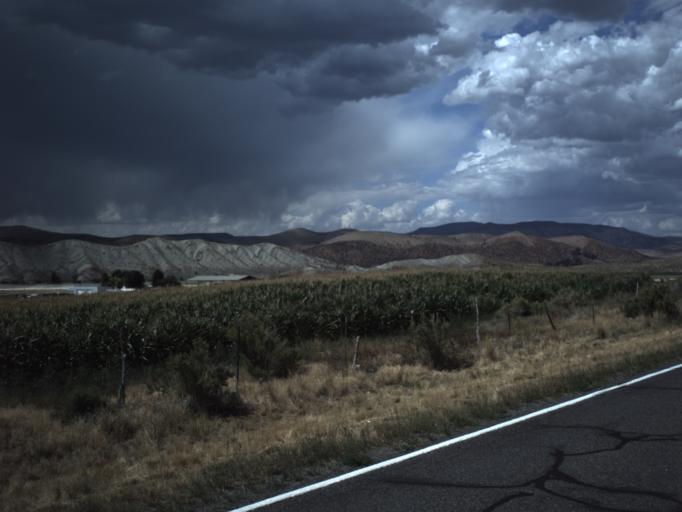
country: US
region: Utah
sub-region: Sanpete County
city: Gunnison
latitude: 39.1652
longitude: -111.7061
